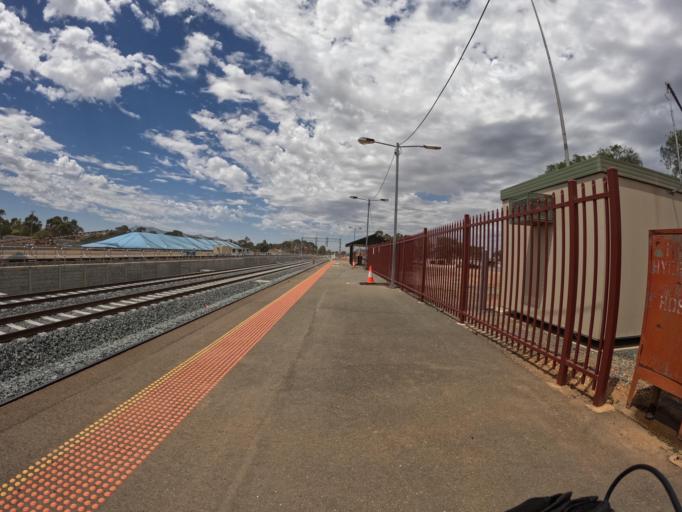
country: AU
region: Victoria
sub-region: Greater Shepparton
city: Shepparton
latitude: -36.6128
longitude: 145.2406
